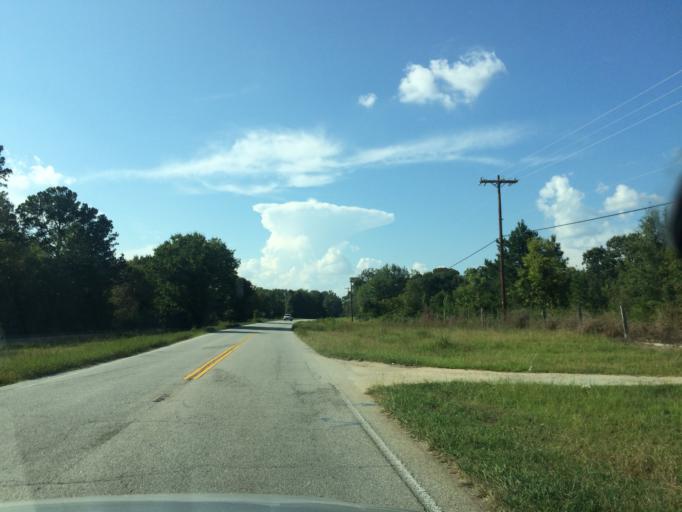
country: US
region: South Carolina
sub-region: Laurens County
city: Laurens
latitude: 34.5382
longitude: -82.0633
